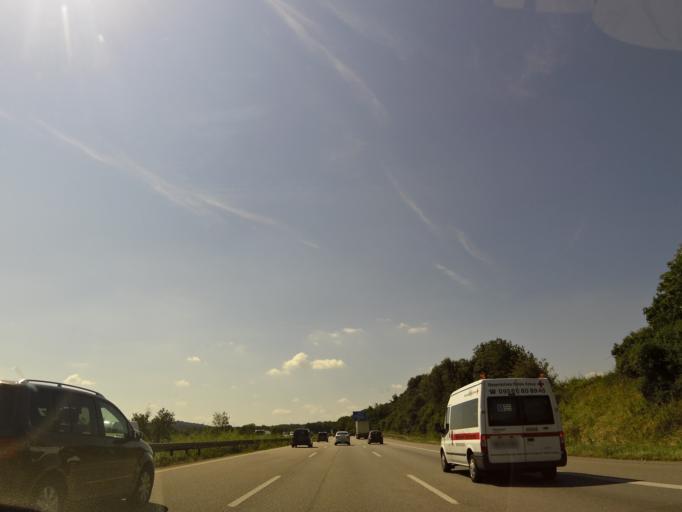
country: DE
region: Bavaria
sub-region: Upper Bavaria
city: Reichertshofen
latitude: 48.6512
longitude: 11.5140
